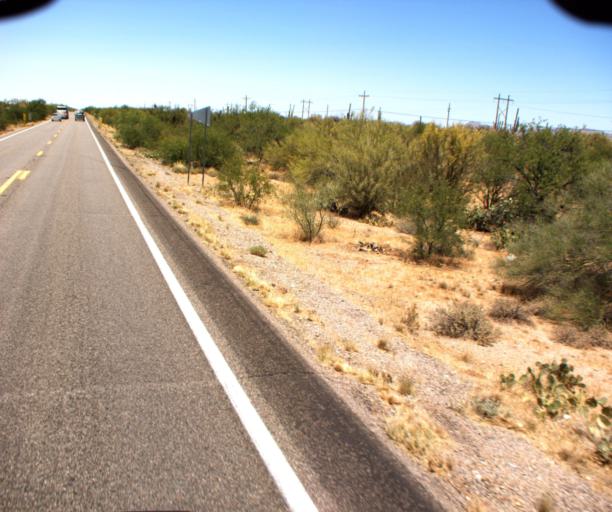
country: US
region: Arizona
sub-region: Pima County
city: Catalina
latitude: 32.7269
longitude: -111.1126
